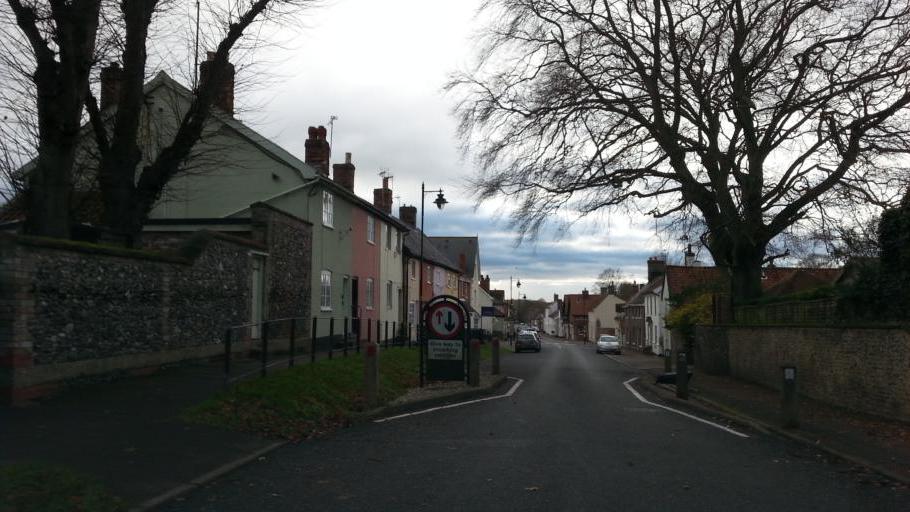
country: GB
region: England
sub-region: Suffolk
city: Ixworth
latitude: 52.3007
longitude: 0.8350
